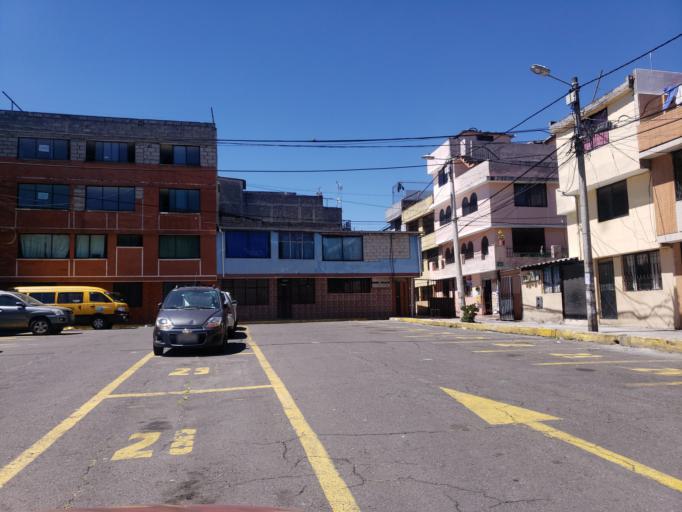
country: EC
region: Pichincha
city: Quito
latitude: -0.2655
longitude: -78.5382
